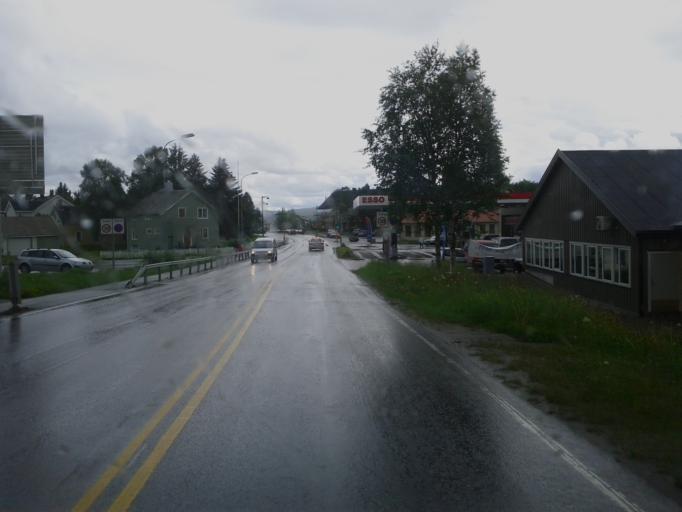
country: NO
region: Sor-Trondelag
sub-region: Roros
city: Roros
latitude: 62.5764
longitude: 11.3774
